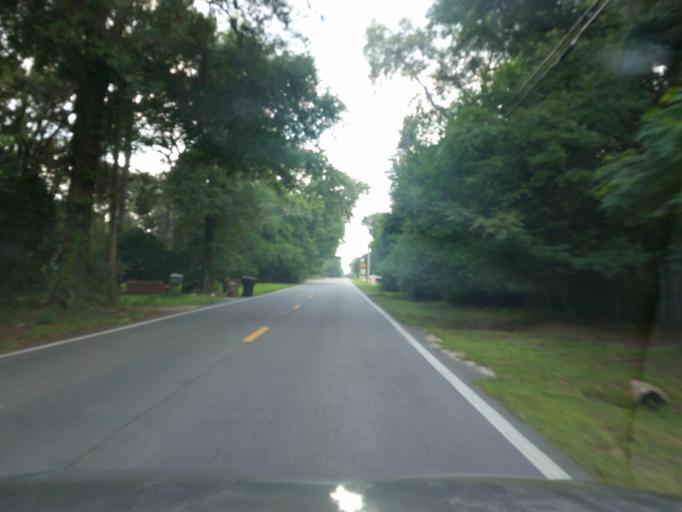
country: US
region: Florida
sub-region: Escambia County
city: Ferry Pass
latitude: 30.4938
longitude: -87.2112
